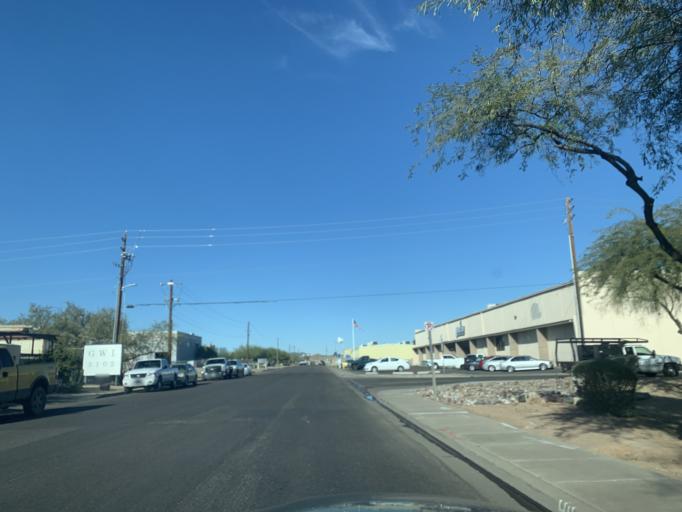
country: US
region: Arizona
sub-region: Maricopa County
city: Tempe Junction
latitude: 33.4180
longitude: -111.9869
